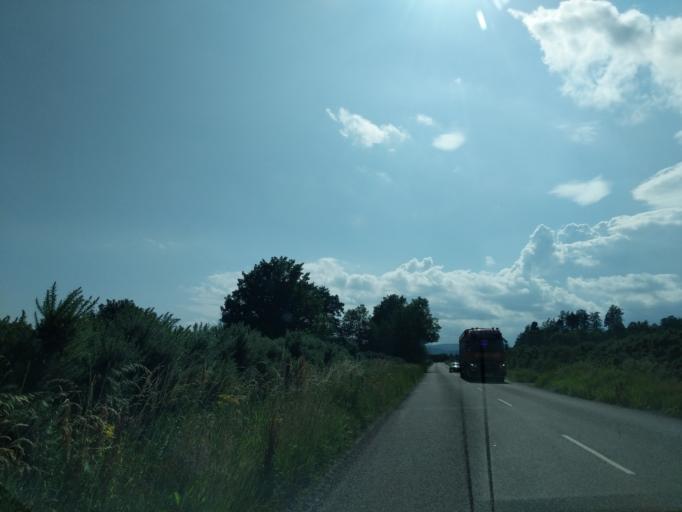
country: GB
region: Scotland
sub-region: Moray
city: Rothes
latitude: 57.5456
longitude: -3.1716
